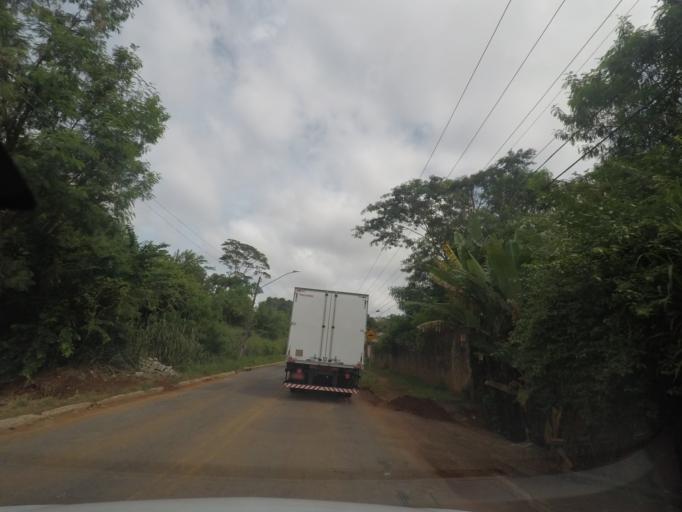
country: BR
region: Goias
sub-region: Goiania
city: Goiania
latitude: -16.6510
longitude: -49.2058
